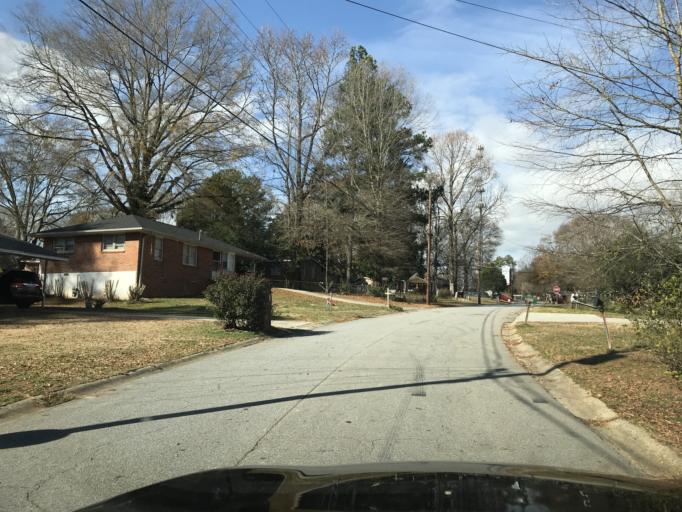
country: US
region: Georgia
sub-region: Clayton County
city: Forest Park
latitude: 33.5891
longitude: -84.3752
